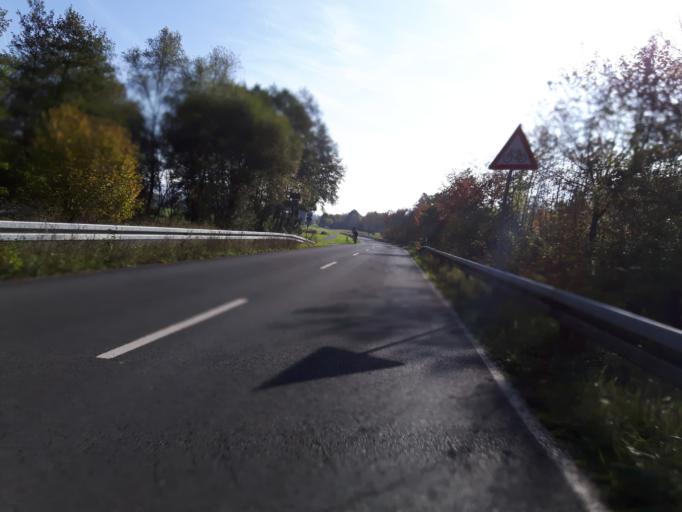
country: DE
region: Bavaria
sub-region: Regierungsbezirk Unterfranken
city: Worth am Main
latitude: 49.8061
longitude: 9.1370
